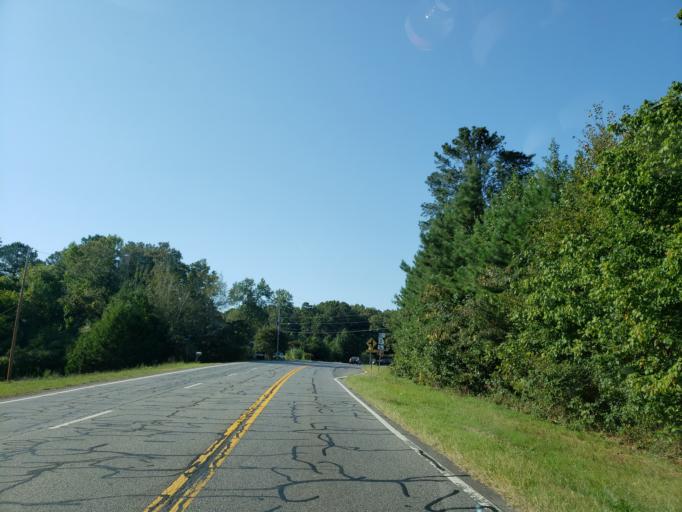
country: US
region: Georgia
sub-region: Whitfield County
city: Varnell
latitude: 34.8966
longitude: -84.9758
